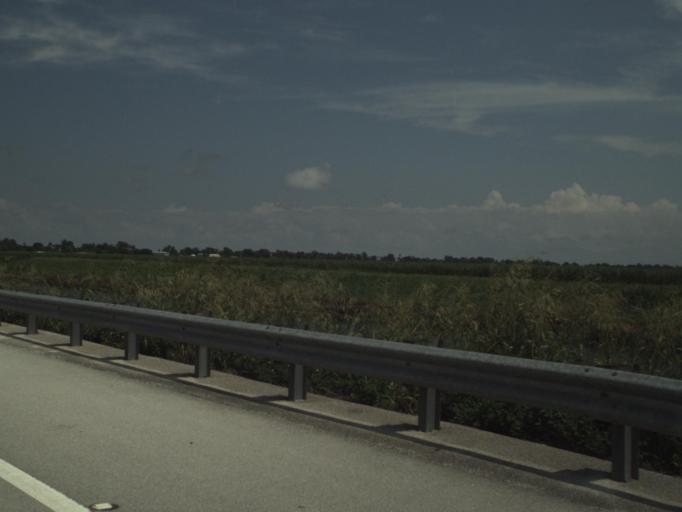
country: US
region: Florida
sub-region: Palm Beach County
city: Pahokee
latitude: 26.8548
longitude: -80.6194
